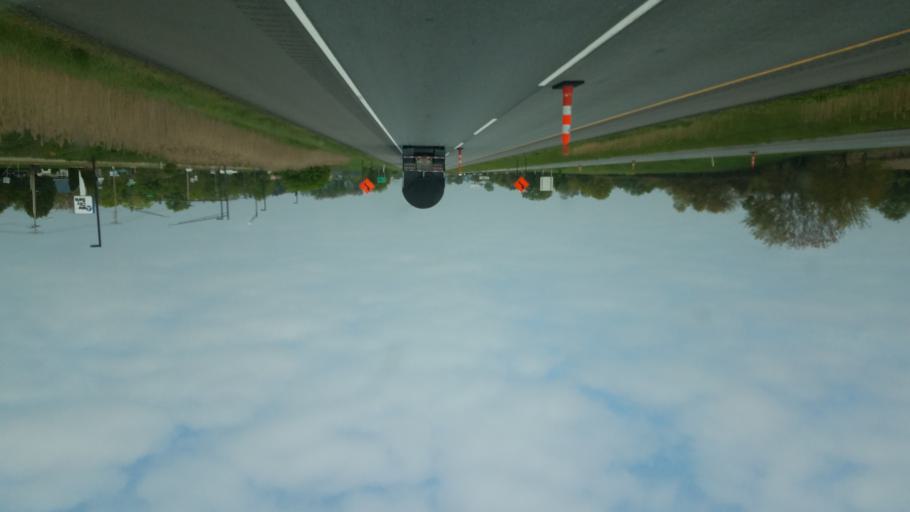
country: US
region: Indiana
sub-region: Saint Joseph County
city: Notre Dame
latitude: 41.7225
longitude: -86.2745
